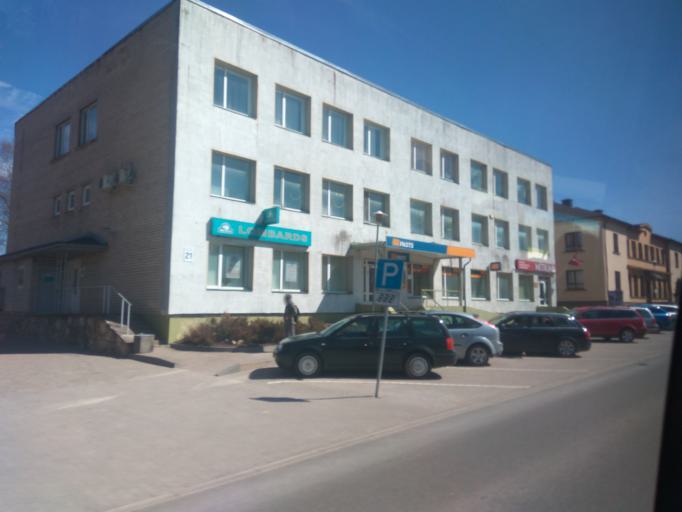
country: LV
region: Aluksnes Rajons
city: Aluksne
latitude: 57.4249
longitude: 27.0454
